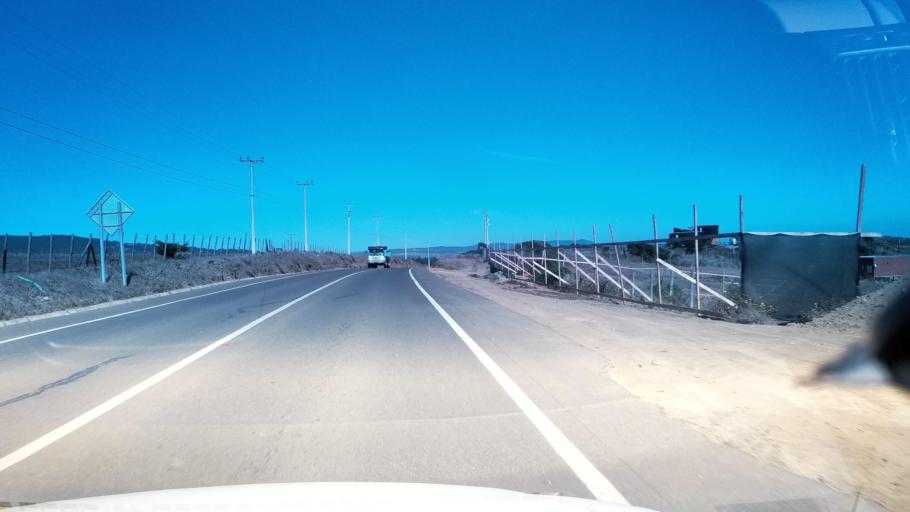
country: CL
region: O'Higgins
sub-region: Provincia de Colchagua
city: Santa Cruz
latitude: -34.4427
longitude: -72.0327
